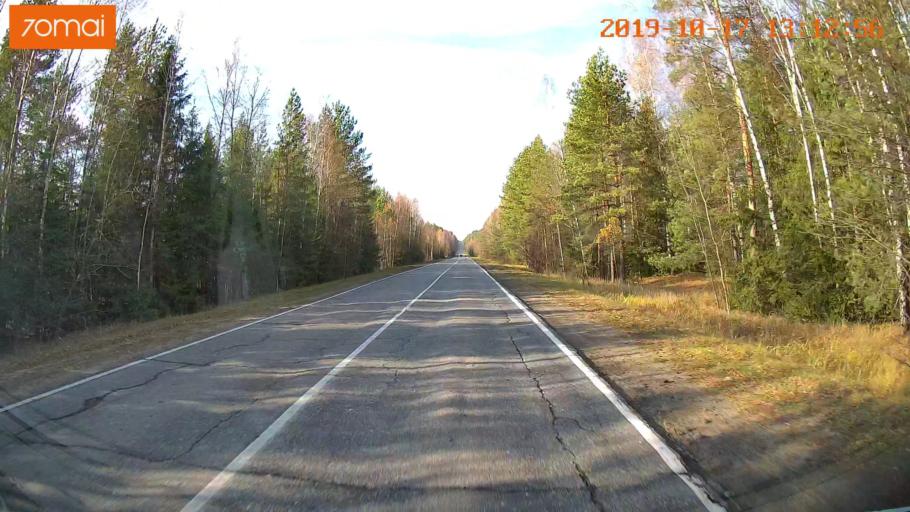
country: RU
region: Rjazan
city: Gus'-Zheleznyy
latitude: 55.0408
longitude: 41.2019
